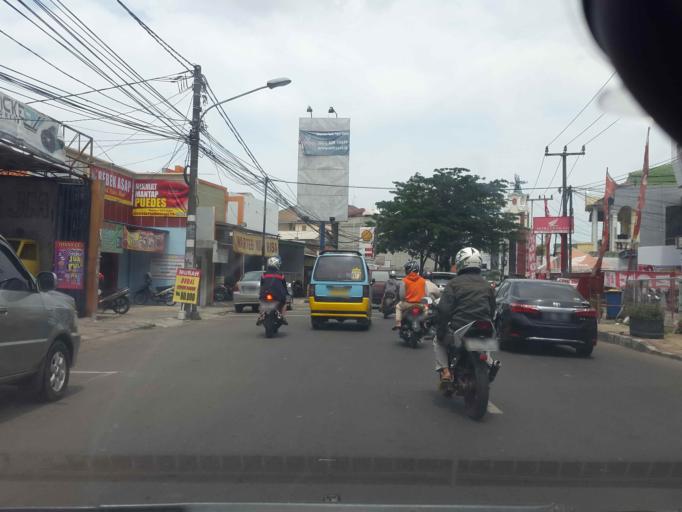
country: ID
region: Banten
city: Tangerang
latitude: -6.1733
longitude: 106.6253
